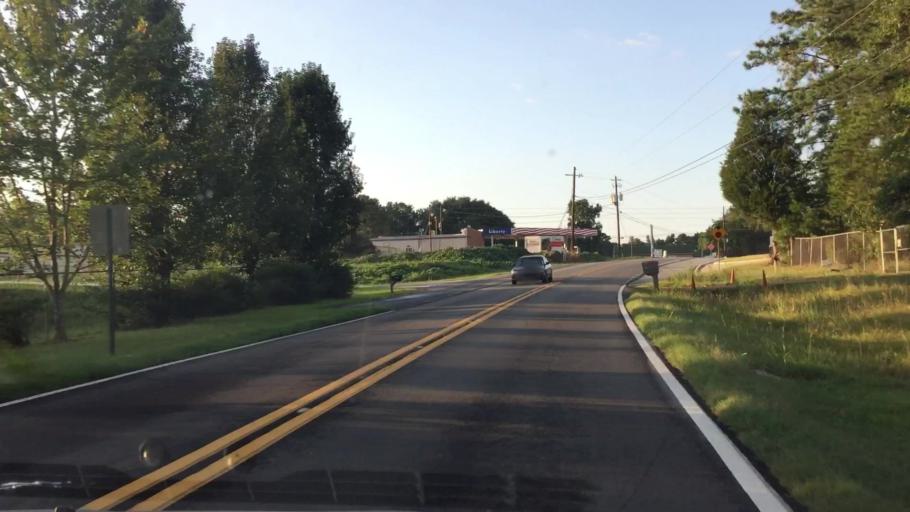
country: US
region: Georgia
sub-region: Henry County
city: McDonough
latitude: 33.4815
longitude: -84.1949
